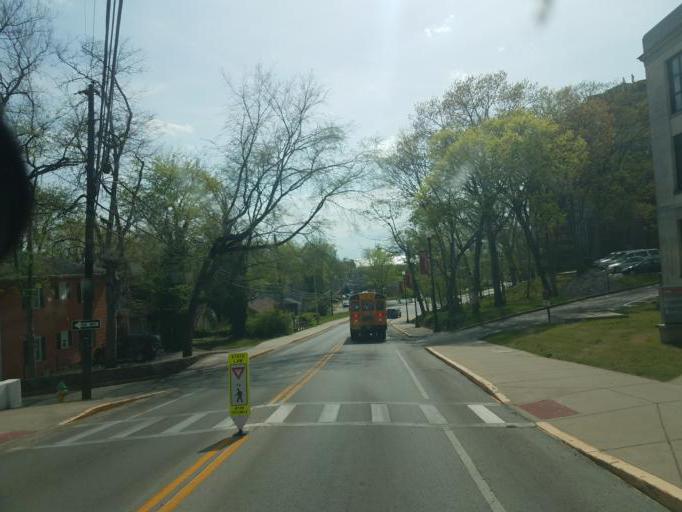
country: US
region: Kentucky
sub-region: Warren County
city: Bowling Green
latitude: 36.9859
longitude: -86.4511
